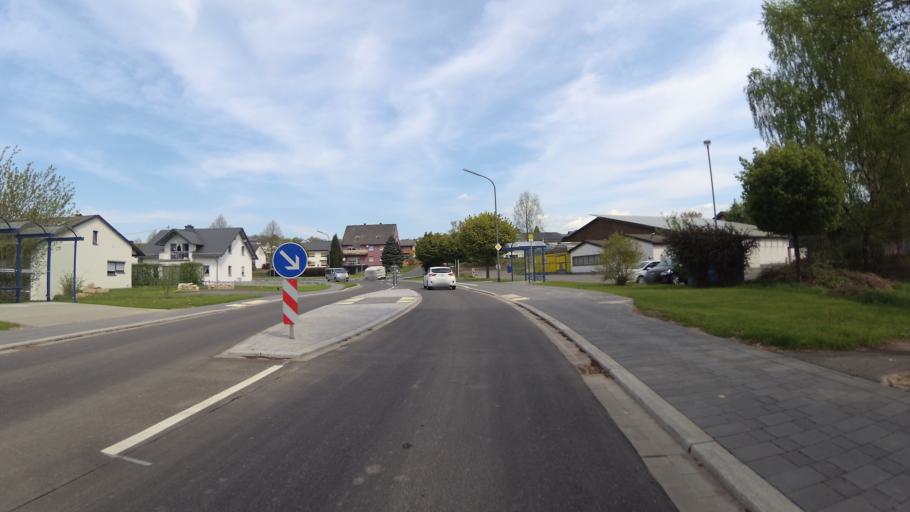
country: DE
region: Rheinland-Pfalz
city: Longkamp
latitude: 49.8591
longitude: 7.1146
